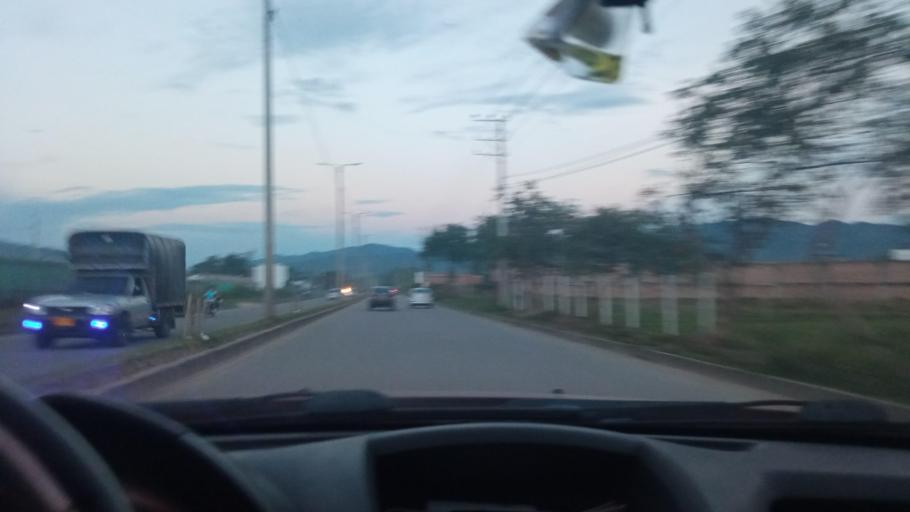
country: CO
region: Huila
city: Pitalito
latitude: 1.8501
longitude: -76.0633
